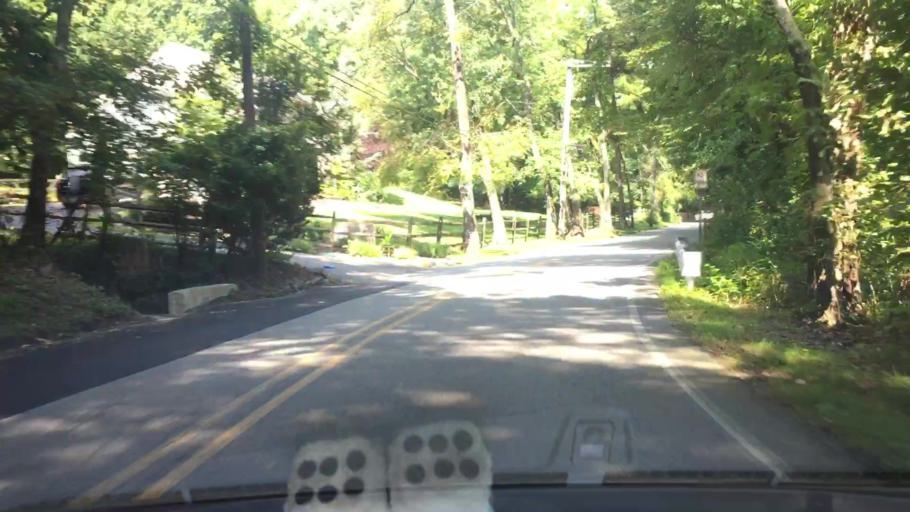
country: US
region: Pennsylvania
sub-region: Delaware County
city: Media
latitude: 39.9032
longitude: -75.3939
